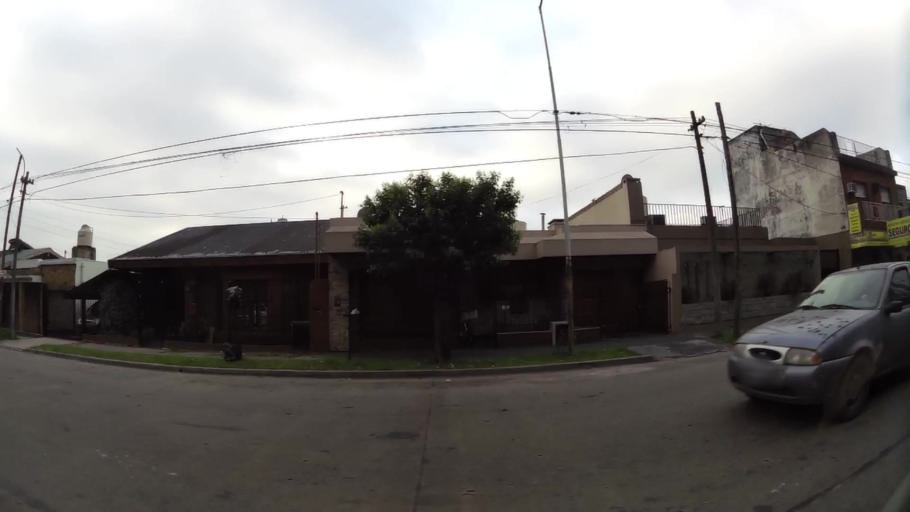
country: AR
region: Buenos Aires
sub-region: Partido de Moron
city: Moron
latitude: -34.6559
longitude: -58.5893
